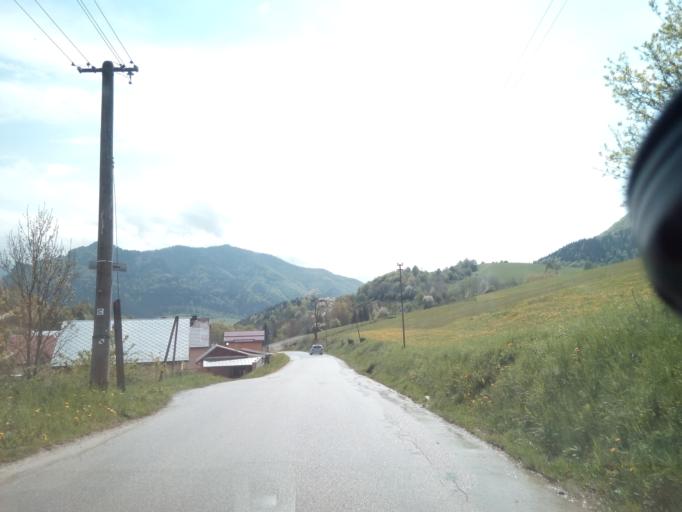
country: SK
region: Zilinsky
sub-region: Okres Zilina
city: Terchova
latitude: 49.2741
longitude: 19.0392
